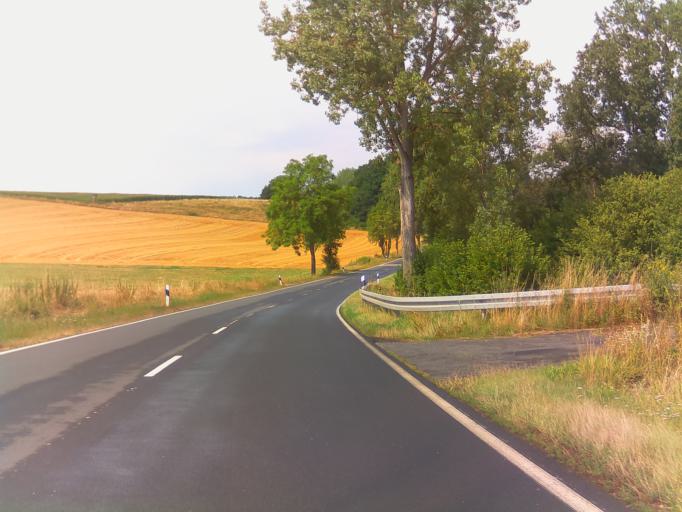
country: DE
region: Hesse
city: Grebenau
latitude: 50.7011
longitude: 9.4468
